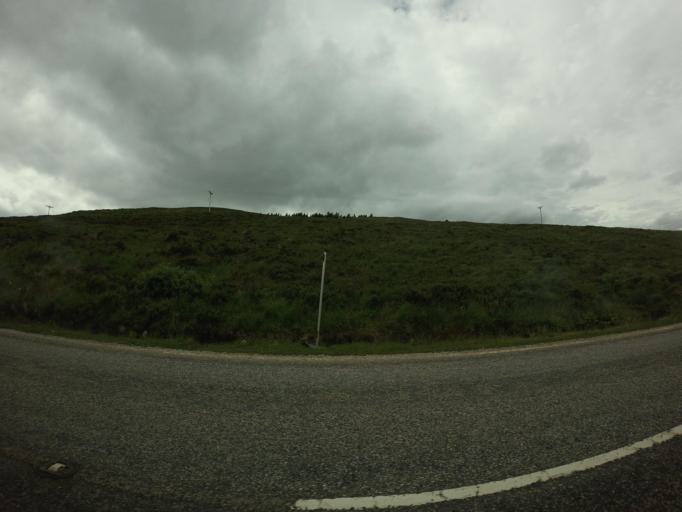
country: GB
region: Scotland
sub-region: Highland
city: Ullapool
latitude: 57.7013
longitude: -4.8142
